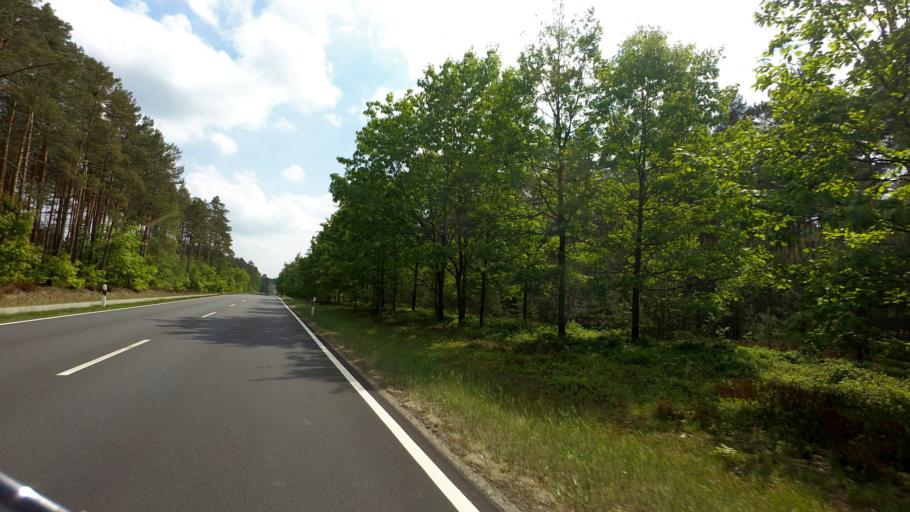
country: DE
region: Saxony
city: Niesky
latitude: 51.3412
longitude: 14.8081
